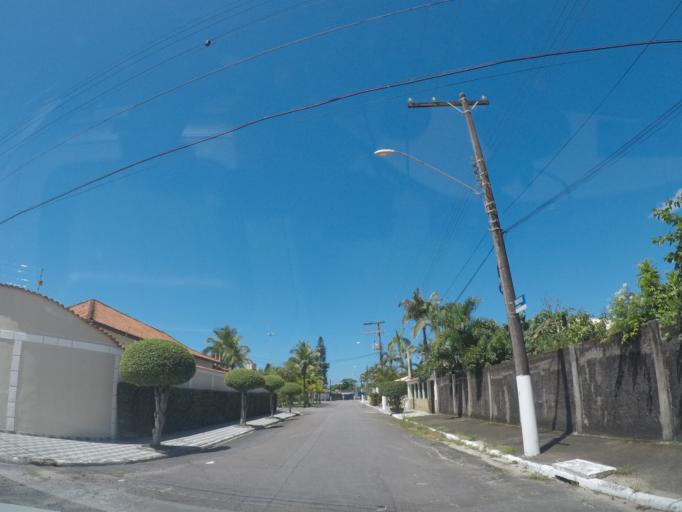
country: BR
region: Sao Paulo
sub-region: Mongagua
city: Mongagua
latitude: -24.0735
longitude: -46.5779
